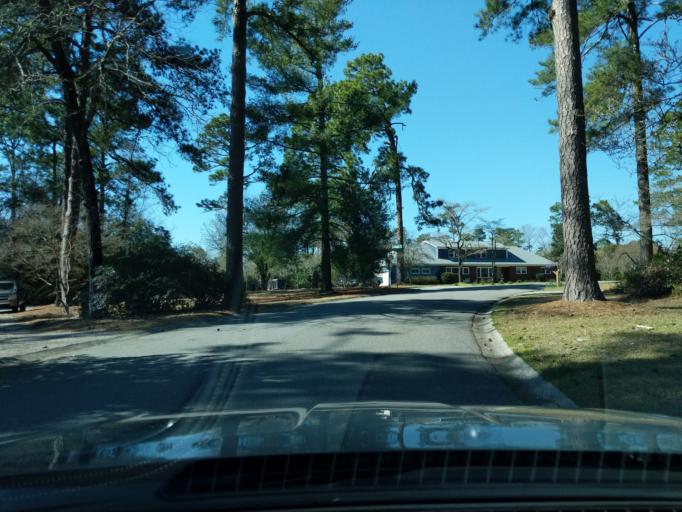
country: US
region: South Carolina
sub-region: Aiken County
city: Aiken
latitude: 33.5321
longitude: -81.7378
